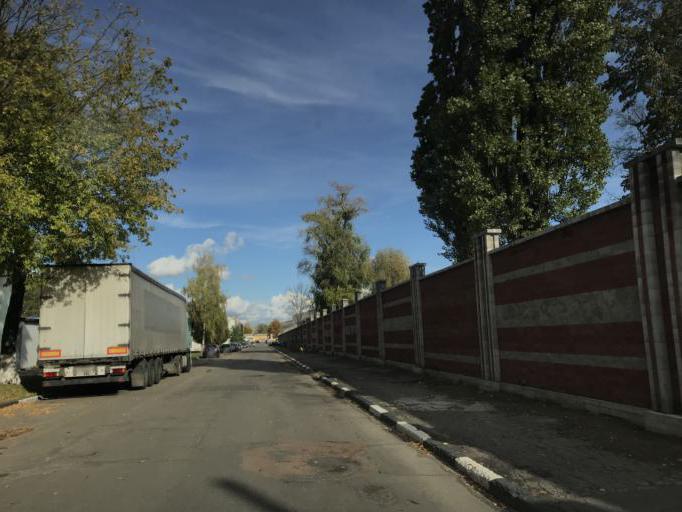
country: BY
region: Gomel
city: Gomel
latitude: 52.4492
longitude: 30.9737
